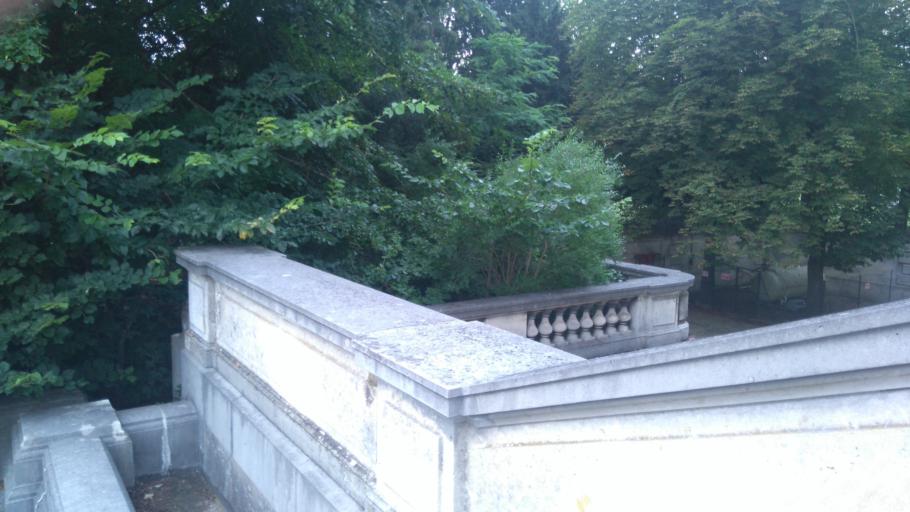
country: FR
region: Picardie
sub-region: Departement de l'Oise
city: Saint-Maximin
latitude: 49.2355
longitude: 2.4521
